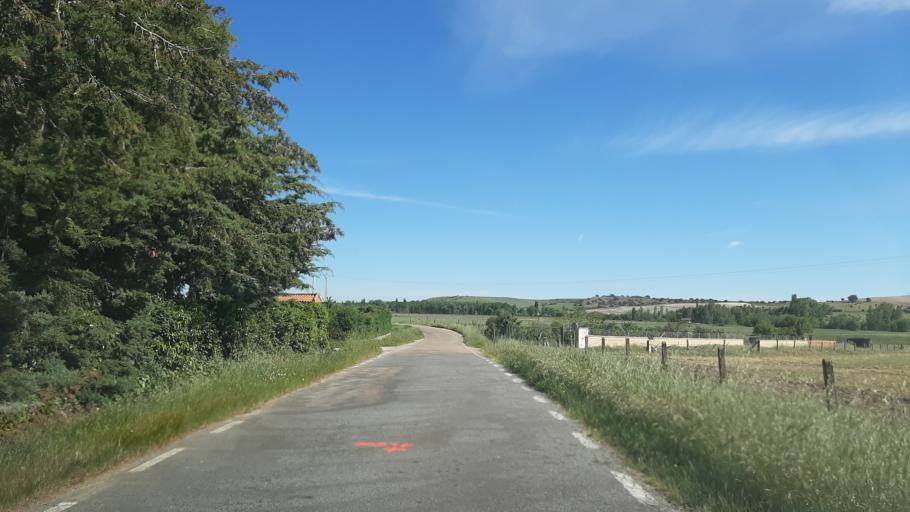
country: ES
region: Castille and Leon
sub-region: Provincia de Salamanca
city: Pedrosillo de Alba
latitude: 40.8083
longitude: -5.3806
